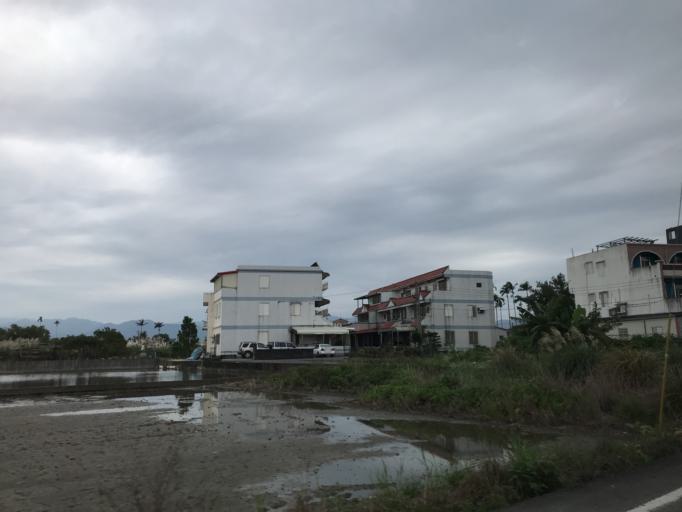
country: TW
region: Taiwan
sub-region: Yilan
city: Yilan
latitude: 24.6888
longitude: 121.7865
